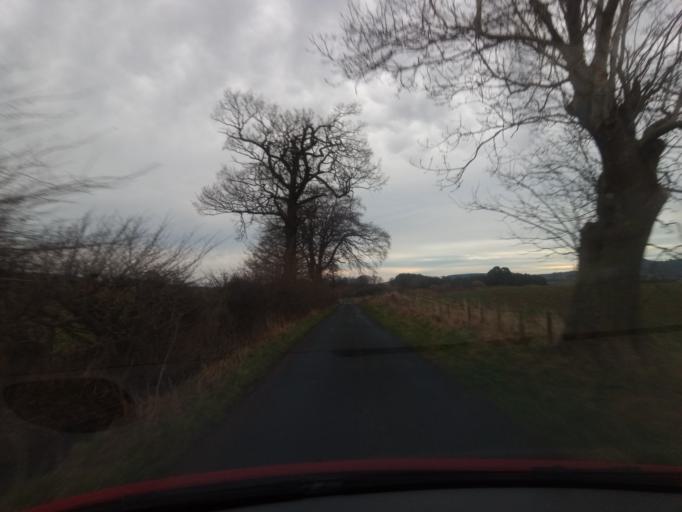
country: GB
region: England
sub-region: Northumberland
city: Wooler
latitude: 55.4933
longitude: -1.9416
